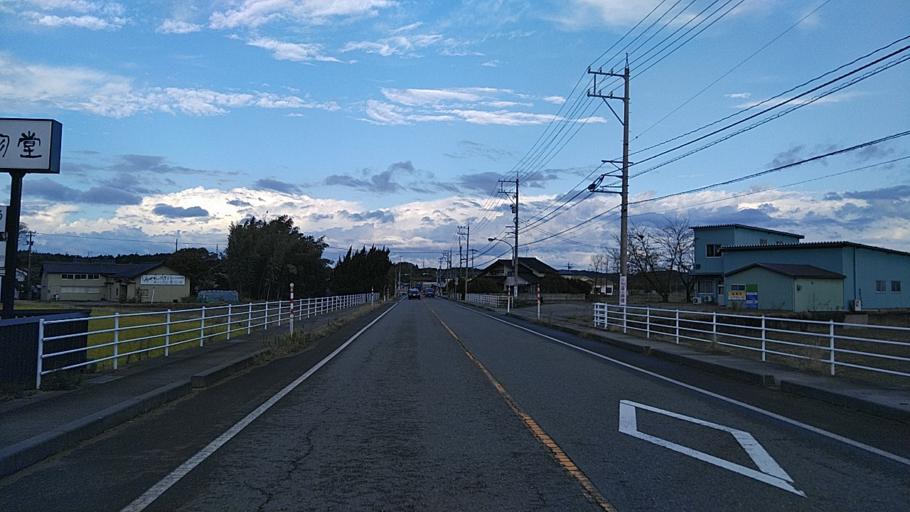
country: JP
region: Ishikawa
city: Komatsu
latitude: 36.2938
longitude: 136.3518
